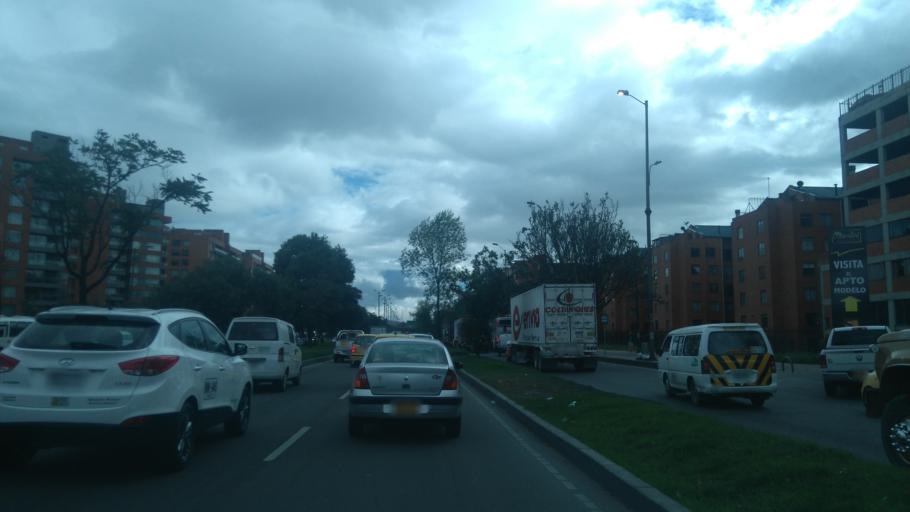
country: CO
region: Bogota D.C.
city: Bogota
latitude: 4.6645
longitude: -74.1134
